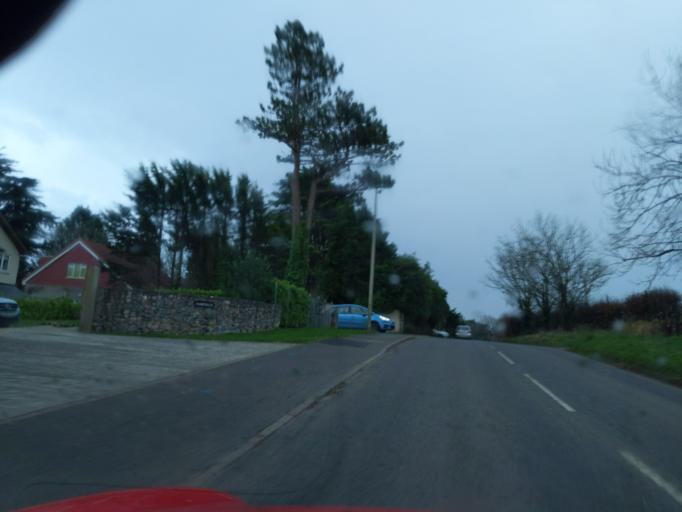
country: GB
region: England
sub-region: Devon
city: Wembury
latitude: 50.3397
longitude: -4.0737
